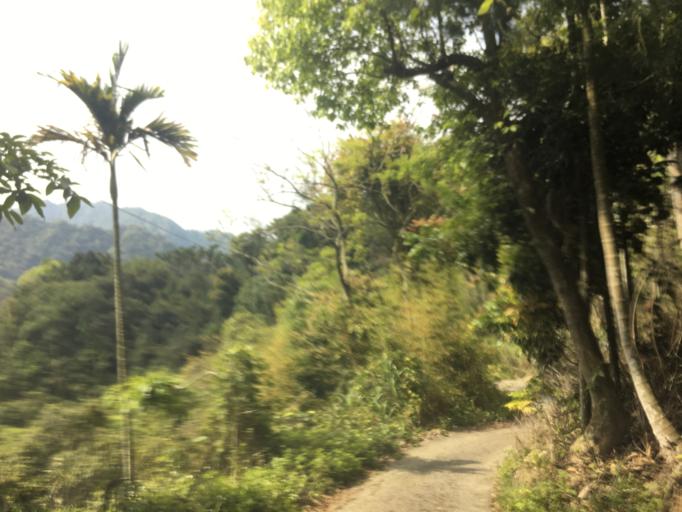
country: TW
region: Taiwan
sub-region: Taichung City
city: Taichung
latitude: 24.1346
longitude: 120.8250
